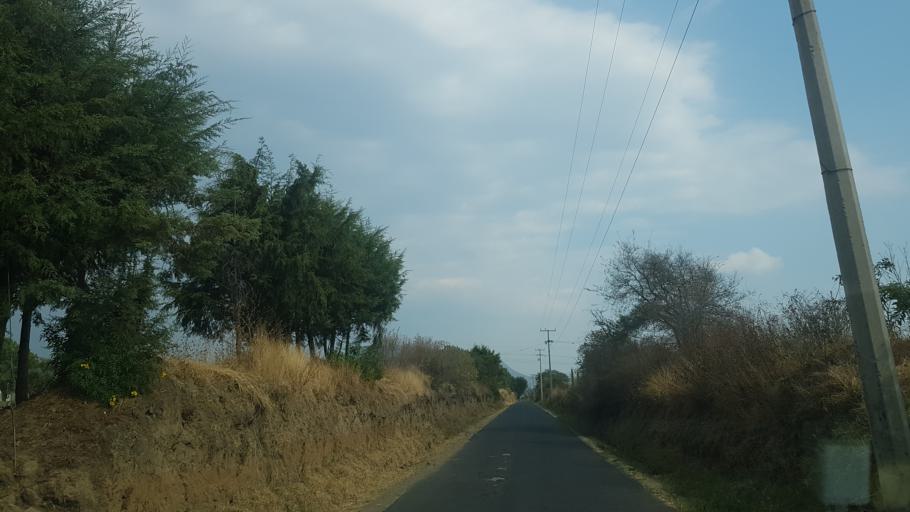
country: MX
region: Puebla
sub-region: Santa Isabel Cholula
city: Santa Ana Acozautla
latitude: 18.9550
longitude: -98.4007
